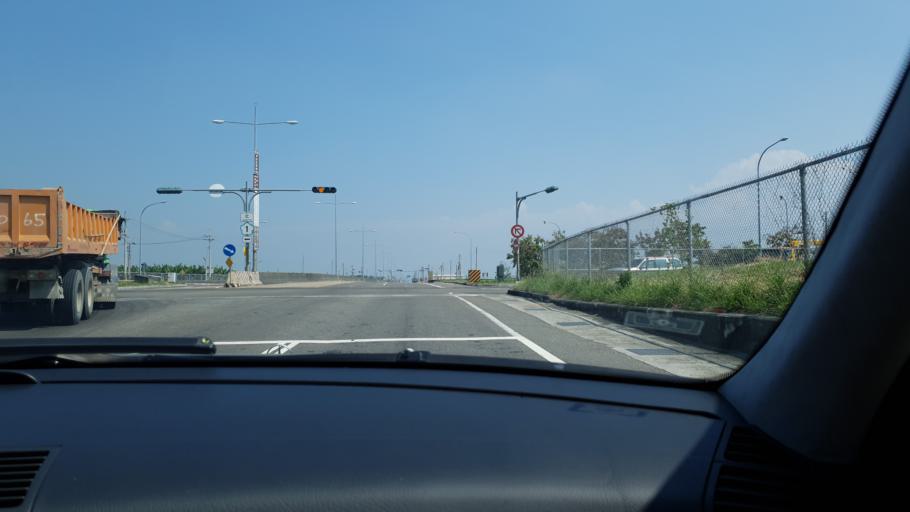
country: TW
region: Taiwan
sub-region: Yunlin
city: Douliu
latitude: 23.7357
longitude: 120.4711
